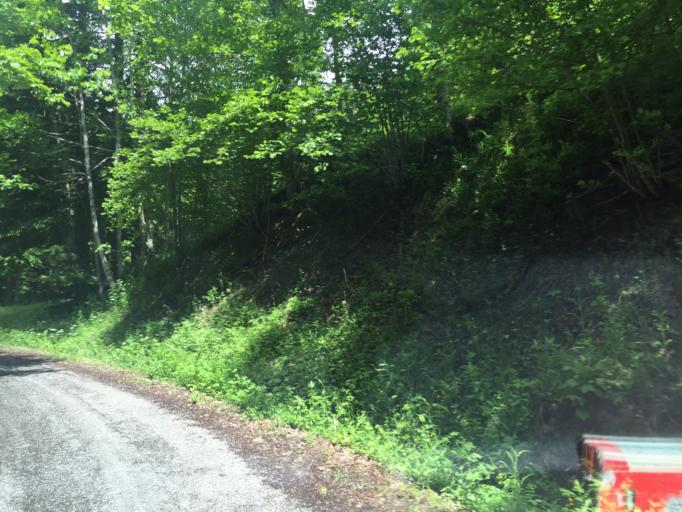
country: FR
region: Rhone-Alpes
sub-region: Departement de la Savoie
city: Coise-Saint-Jean-Pied-Gauthier
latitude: 45.6246
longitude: 6.1275
